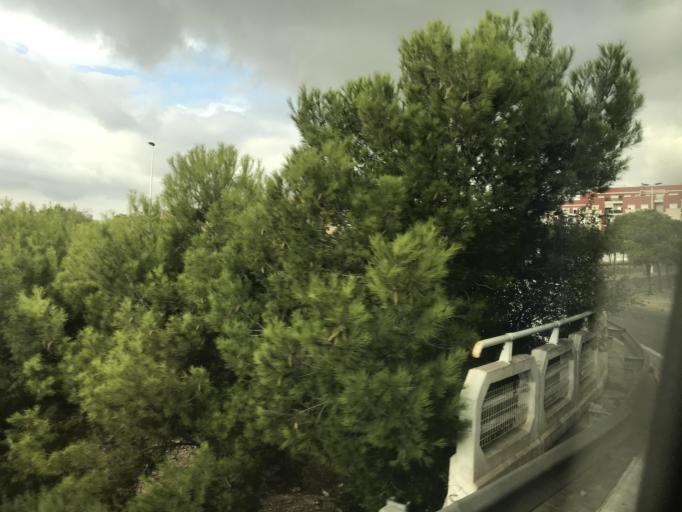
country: ES
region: Valencia
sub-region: Provincia de Alicante
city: Santa Pola
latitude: 38.2003
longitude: -0.5601
